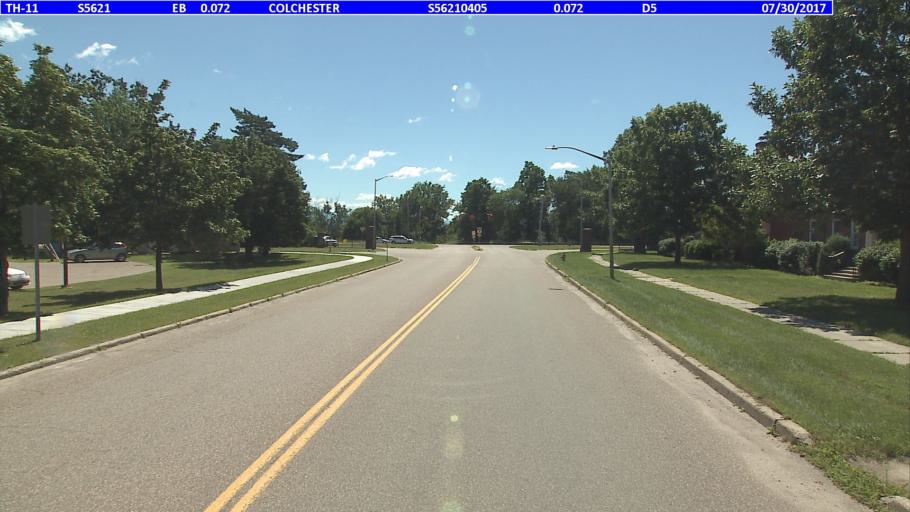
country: US
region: Vermont
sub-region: Chittenden County
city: Winooski
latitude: 44.5023
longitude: -73.1515
